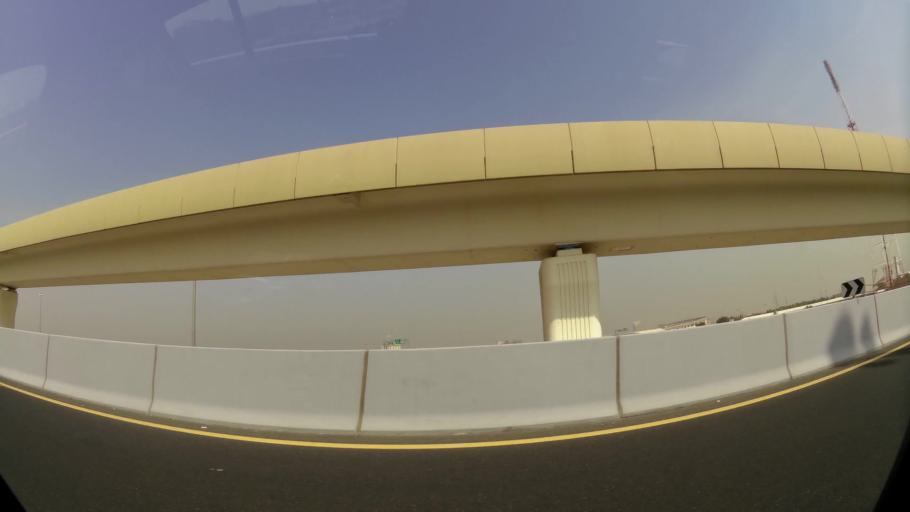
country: KW
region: Al Asimah
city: Ar Rabiyah
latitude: 29.3096
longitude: 47.8881
